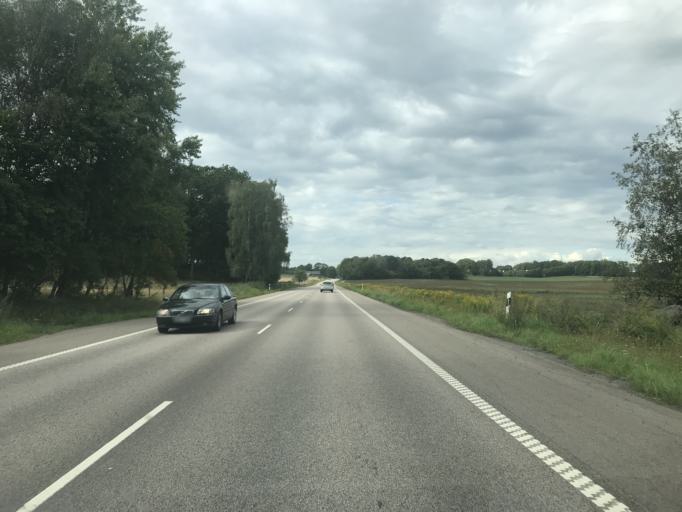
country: SE
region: Skane
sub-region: Hassleholms Kommun
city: Hassleholm
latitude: 56.1343
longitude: 13.8145
